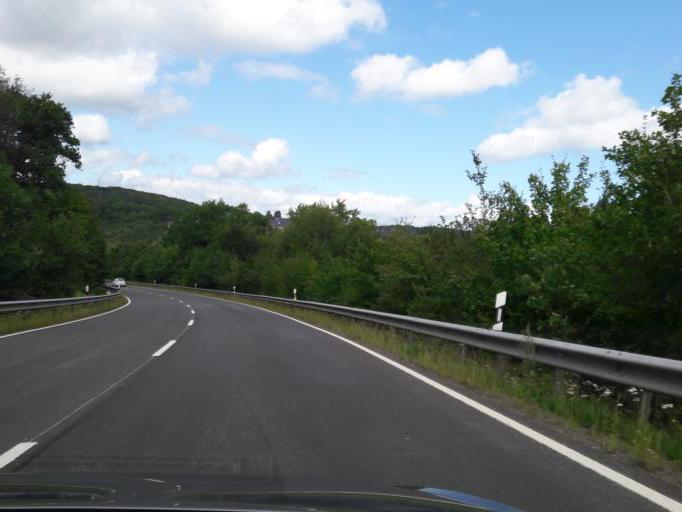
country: DE
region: Rheinland-Pfalz
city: Baumholder
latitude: 49.6133
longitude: 7.3108
